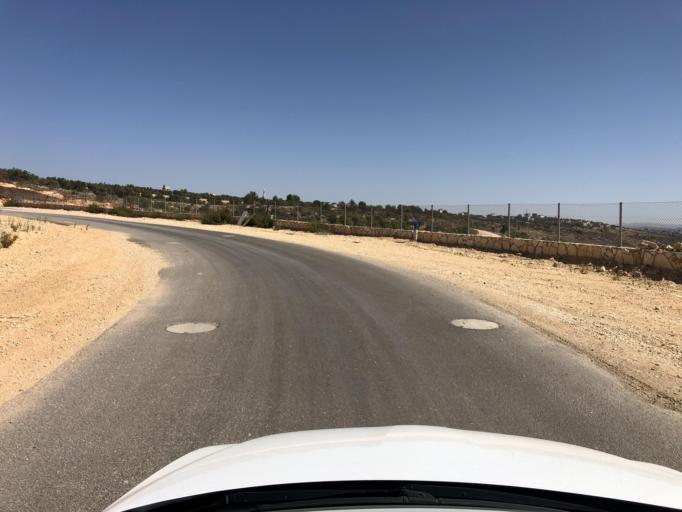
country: PS
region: West Bank
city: Kafr Thulth
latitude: 32.1650
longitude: 35.0301
